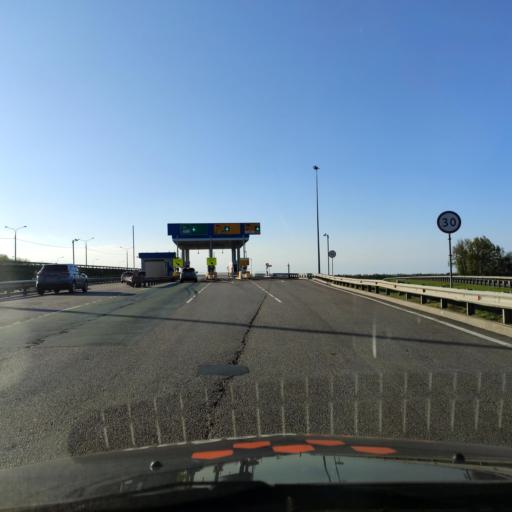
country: RU
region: Lipetsk
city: Yelets
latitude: 52.5437
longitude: 38.7194
